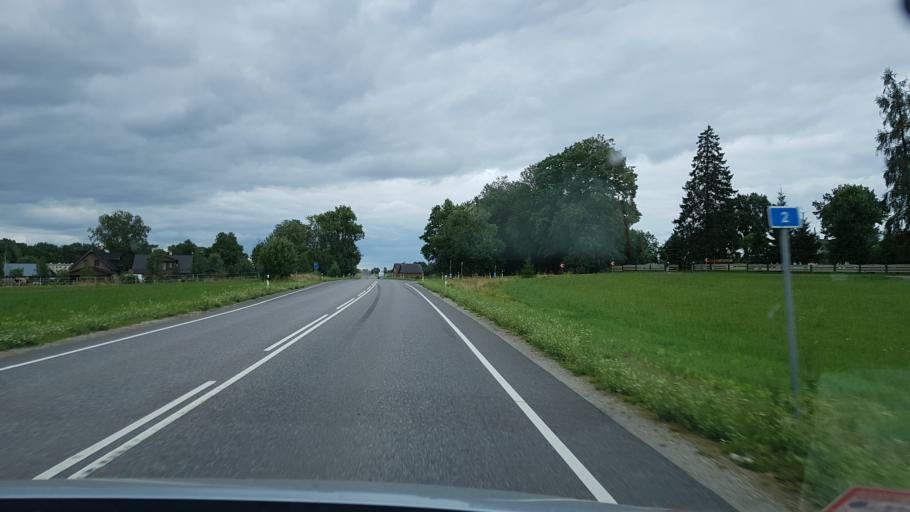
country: EE
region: Tartu
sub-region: Tartu linn
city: Tartu
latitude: 58.4352
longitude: 26.8326
